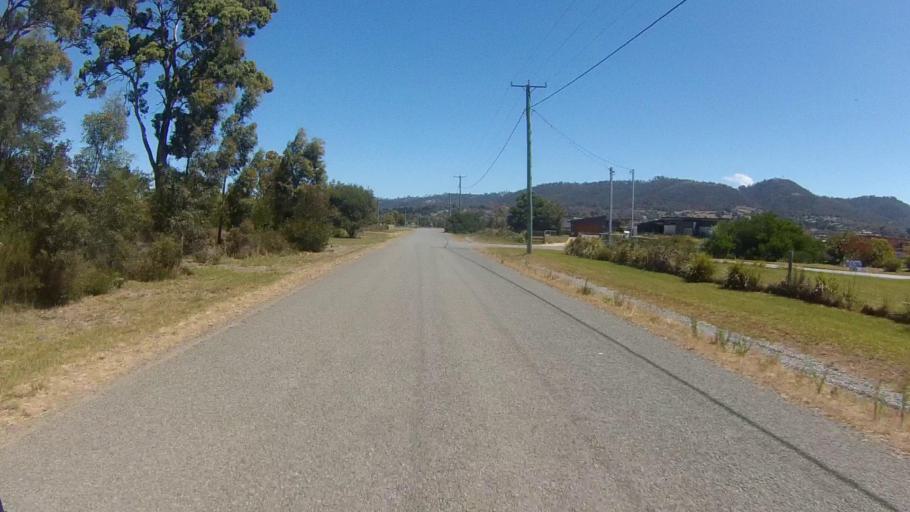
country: AU
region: Tasmania
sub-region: Clarence
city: Seven Mile Beach
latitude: -42.8503
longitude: 147.4925
